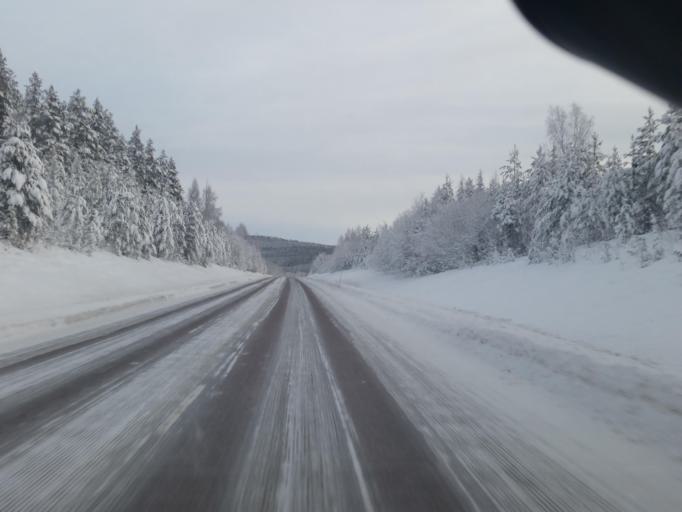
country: SE
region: Norrbotten
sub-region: Alvsbyns Kommun
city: AElvsbyn
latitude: 65.6739
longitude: 21.1810
